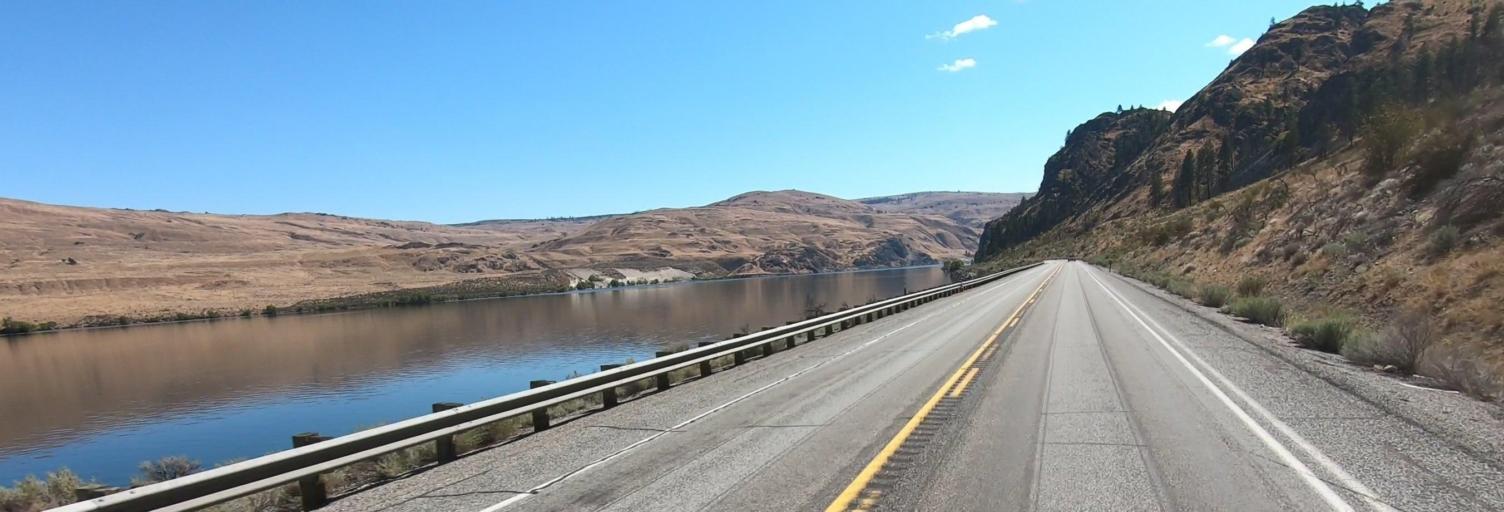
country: US
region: Washington
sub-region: Okanogan County
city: Brewster
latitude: 47.9710
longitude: -119.8866
